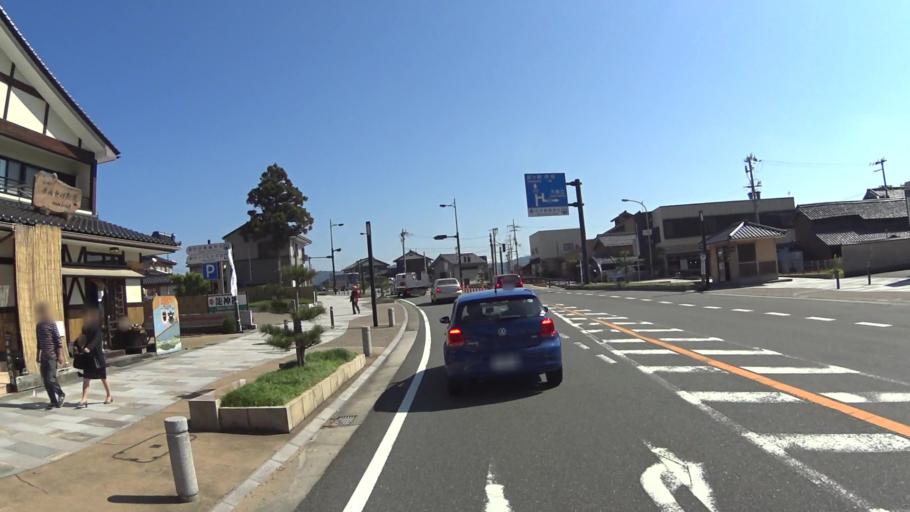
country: JP
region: Kyoto
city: Miyazu
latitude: 35.5837
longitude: 135.1875
